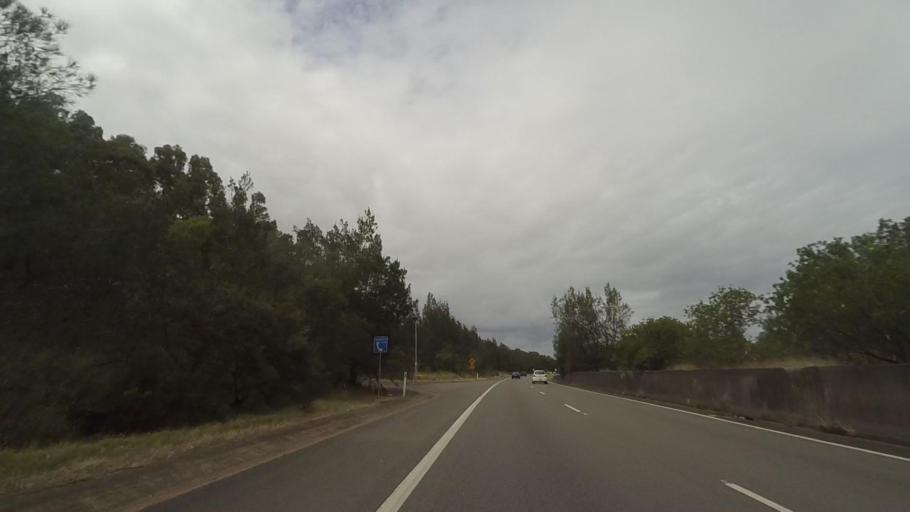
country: AU
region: New South Wales
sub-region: Port Stephens Shire
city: Raymond Terrace
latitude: -32.7483
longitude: 151.7682
